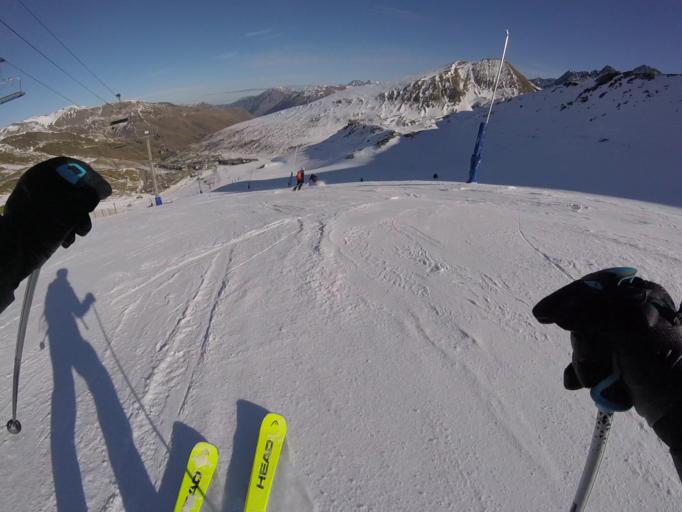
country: AD
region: Encamp
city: Pas de la Casa
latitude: 42.5305
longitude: 1.7229
